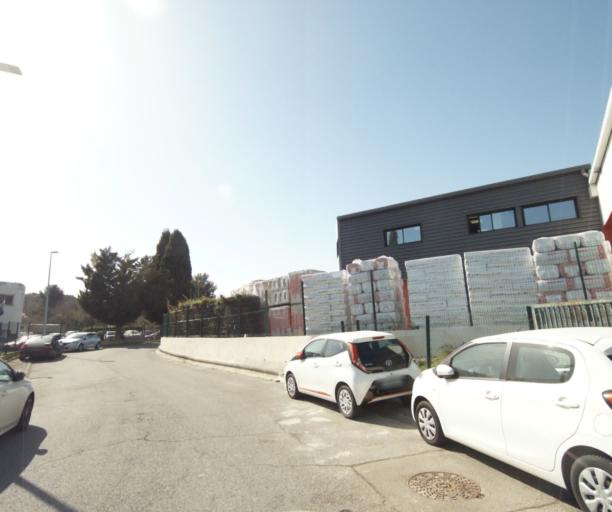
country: FR
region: Provence-Alpes-Cote d'Azur
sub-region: Departement des Bouches-du-Rhone
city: Cabries
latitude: 43.4269
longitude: 5.3962
